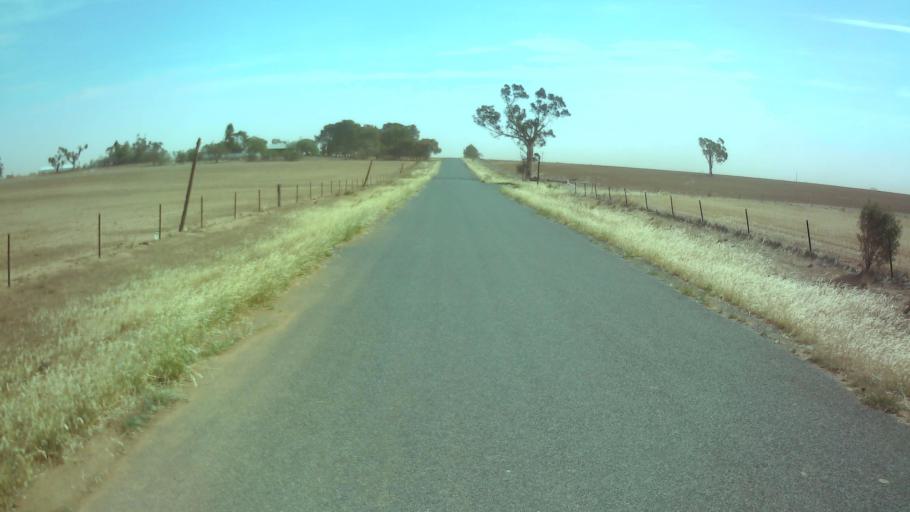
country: AU
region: New South Wales
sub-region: Weddin
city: Grenfell
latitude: -33.7332
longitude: 147.9976
